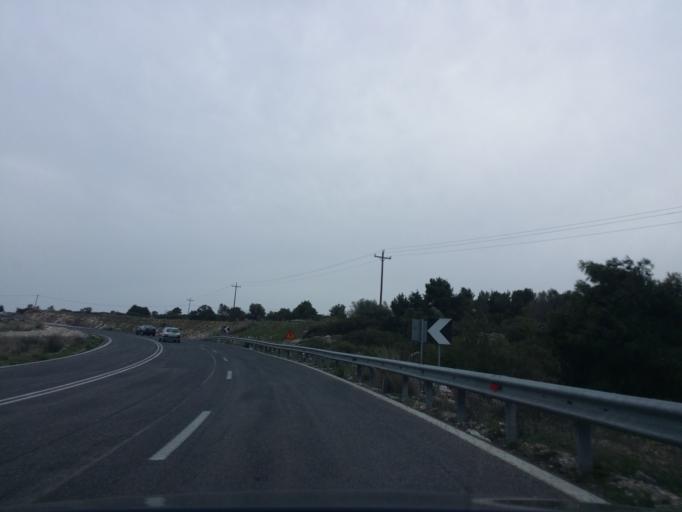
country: GR
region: Attica
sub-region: Nomarchia Dytikis Attikis
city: Vilia
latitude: 38.1585
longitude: 23.4291
